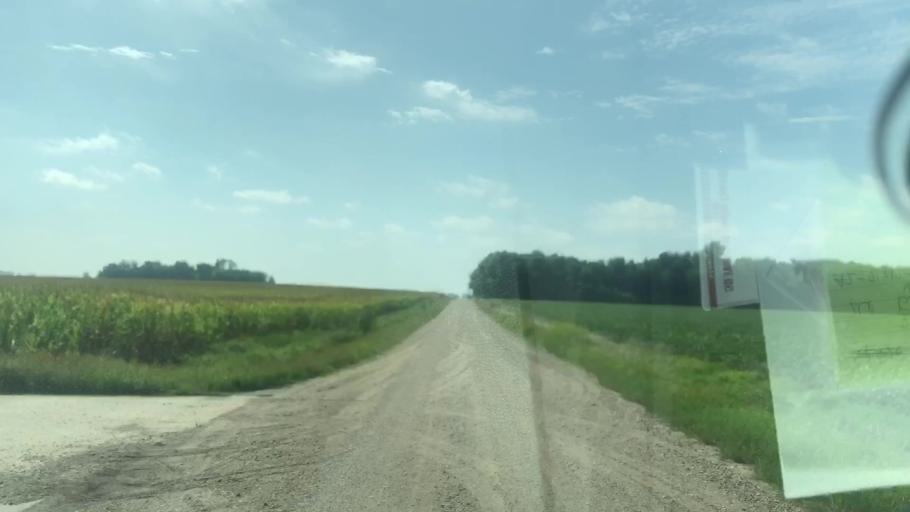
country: US
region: Iowa
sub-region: O'Brien County
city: Sheldon
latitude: 43.1947
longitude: -95.9416
